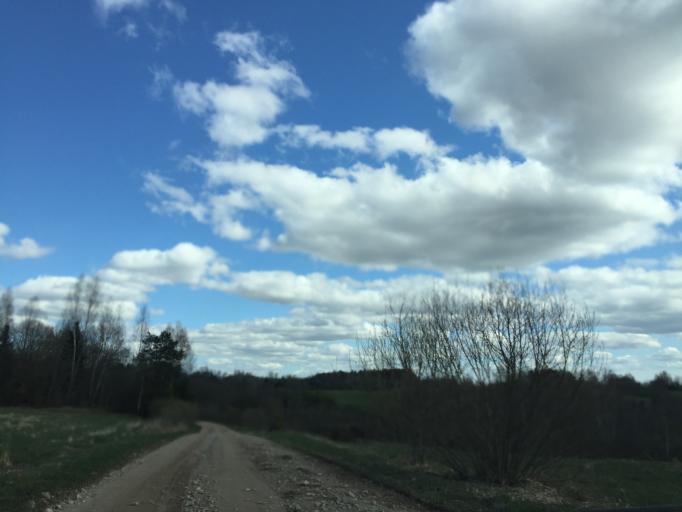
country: LV
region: Rezekne
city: Rezekne
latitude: 56.6638
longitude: 27.2941
